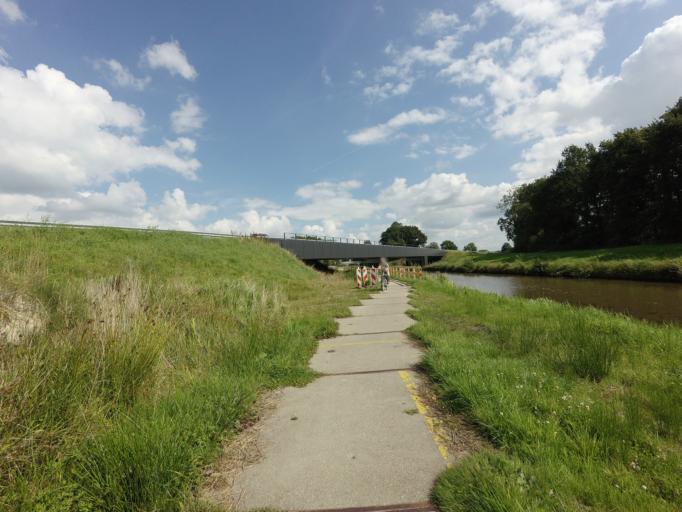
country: NL
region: Friesland
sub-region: Gemeente Heerenveen
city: Jubbega
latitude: 52.9950
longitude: 6.2561
